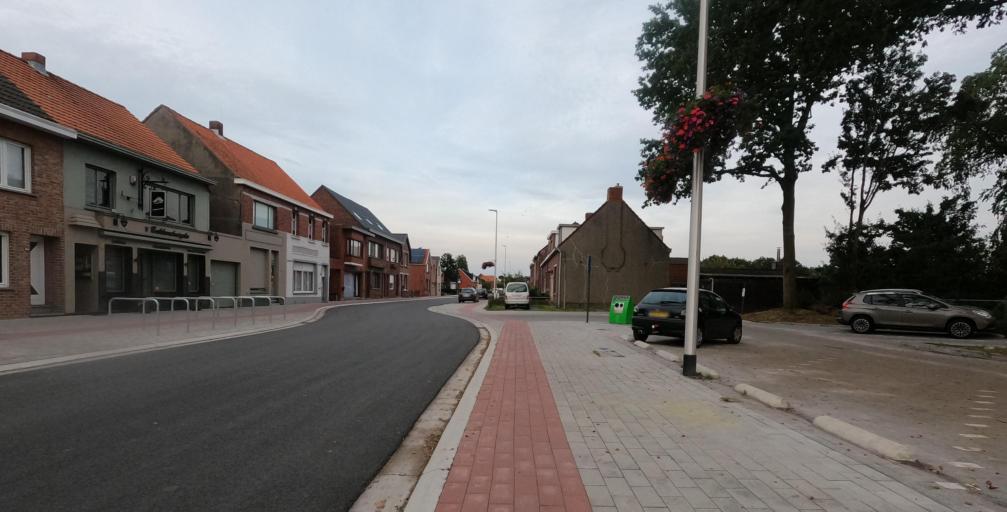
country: BE
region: Flanders
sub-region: Provincie Antwerpen
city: Essen
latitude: 51.4674
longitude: 4.4945
